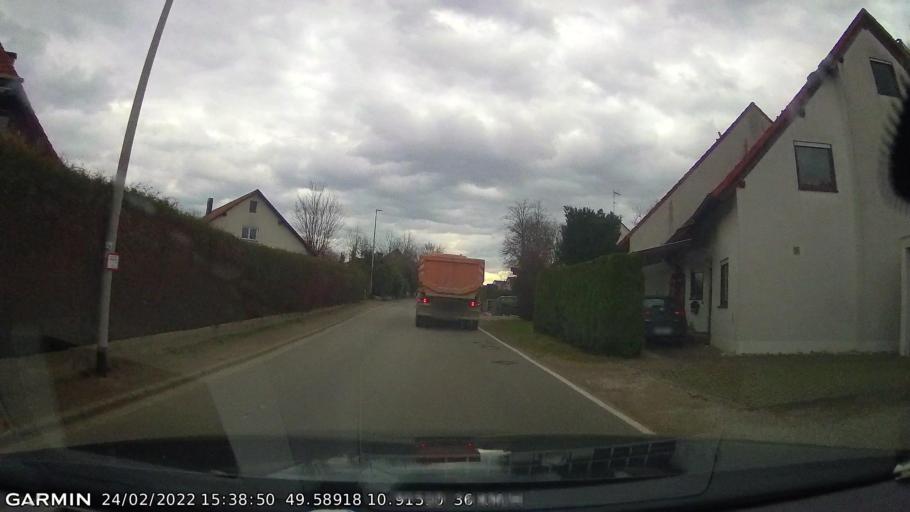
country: DE
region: Bavaria
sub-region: Regierungsbezirk Mittelfranken
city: Herzogenaurach
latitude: 49.5892
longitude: 10.9151
